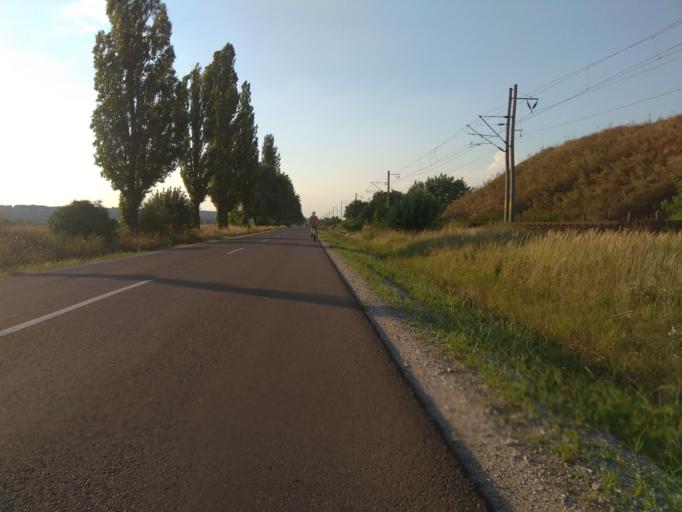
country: HU
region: Borsod-Abauj-Zemplen
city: Nyekladhaza
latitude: 47.9786
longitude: 20.8462
